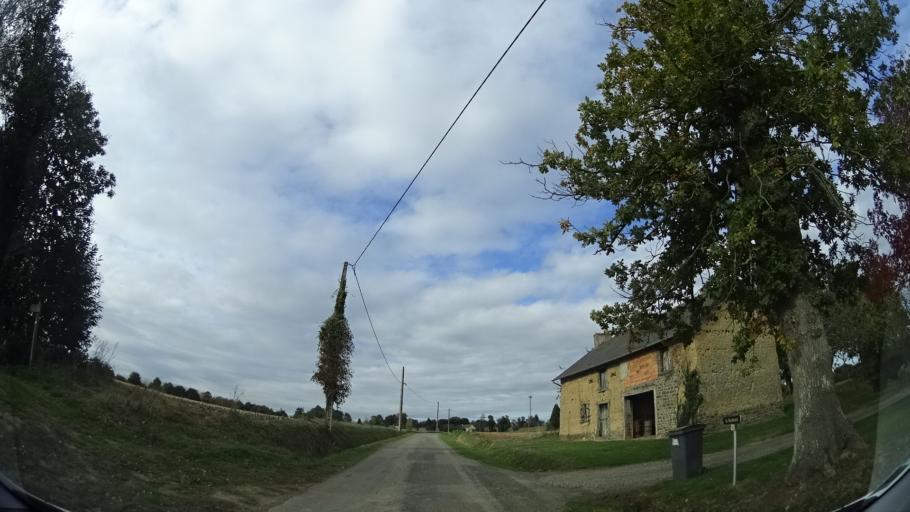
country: FR
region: Brittany
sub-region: Departement d'Ille-et-Vilaine
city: Vignoc
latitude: 48.2398
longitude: -1.7955
